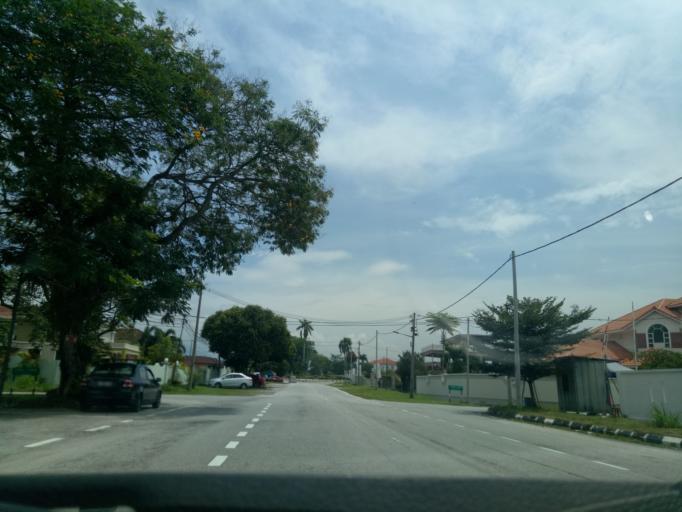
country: MY
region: Perak
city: Ipoh
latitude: 4.6013
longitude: 101.1123
